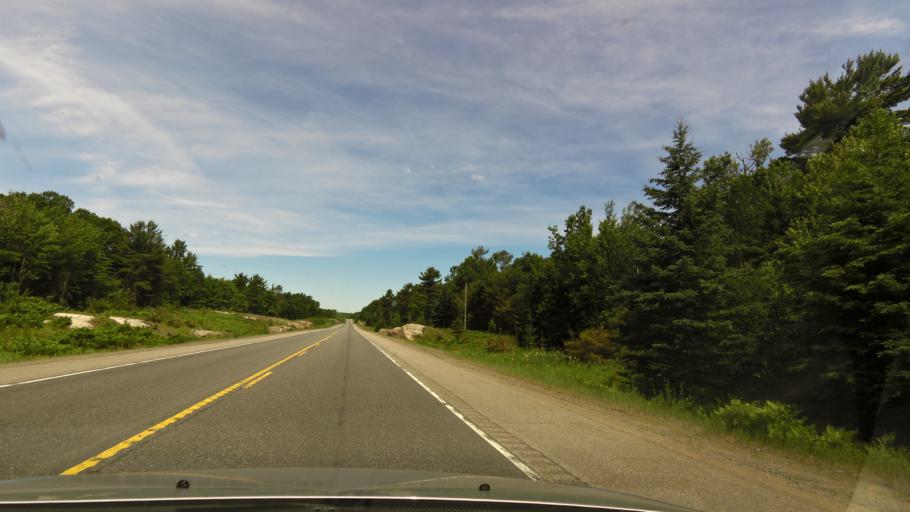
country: CA
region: Ontario
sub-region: Parry Sound District
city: Parry Sound
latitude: 45.4716
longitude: -80.1709
